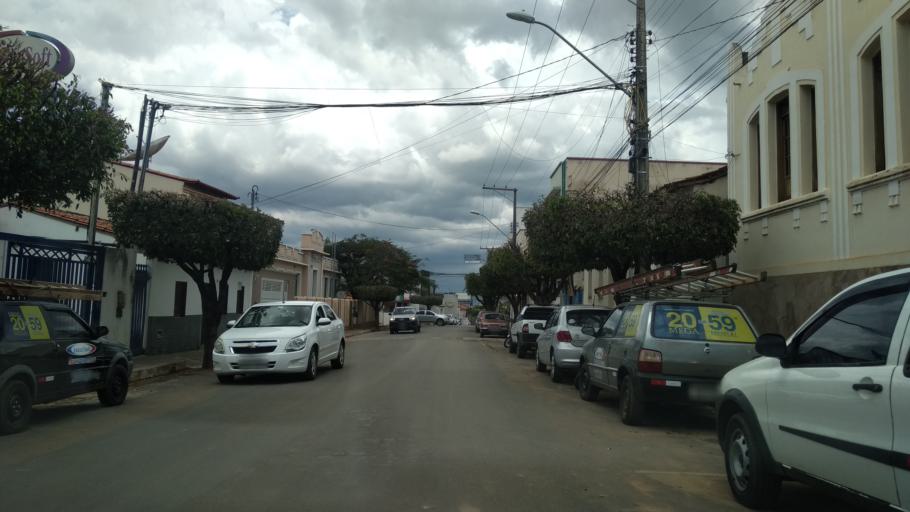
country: BR
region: Bahia
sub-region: Caetite
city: Caetite
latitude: -14.0703
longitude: -42.4905
